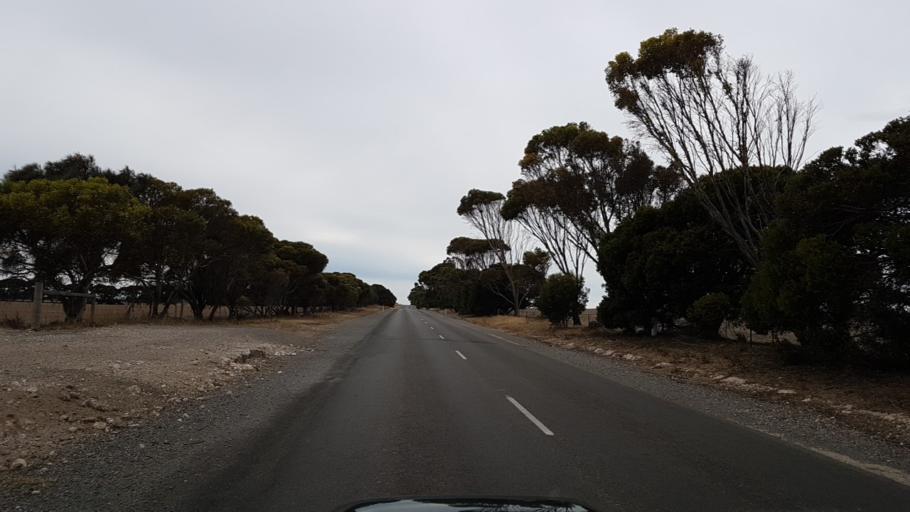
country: AU
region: South Australia
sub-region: Yorke Peninsula
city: Honiton
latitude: -34.9850
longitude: 137.2542
